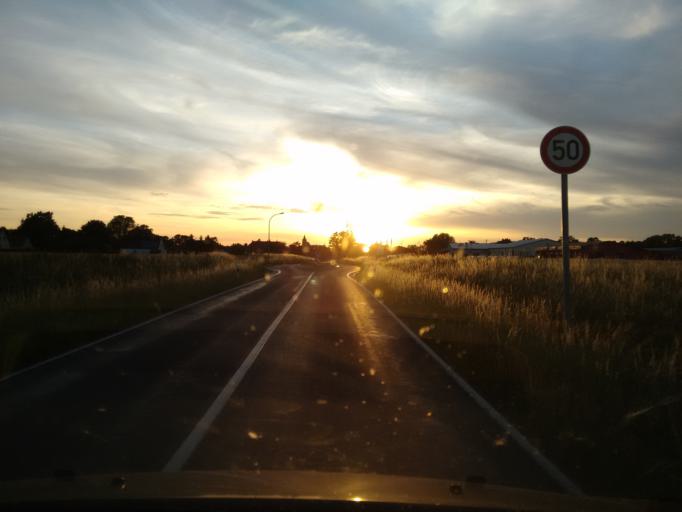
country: DE
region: Brandenburg
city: Beeskow
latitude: 52.1655
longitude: 14.2656
